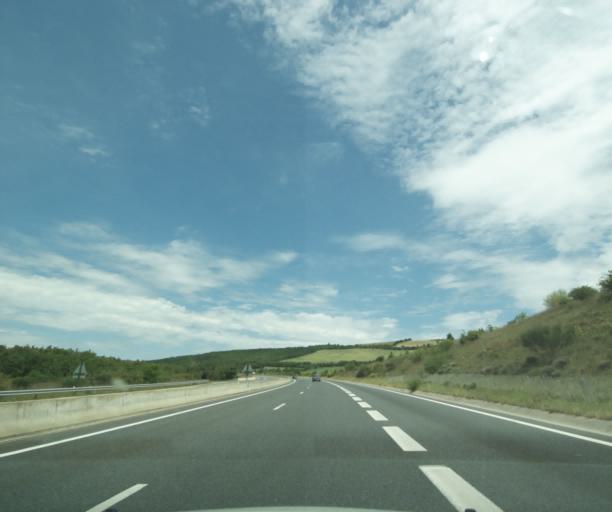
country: FR
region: Midi-Pyrenees
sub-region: Departement de l'Aveyron
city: Severac-le-Chateau
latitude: 44.2161
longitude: 3.0720
